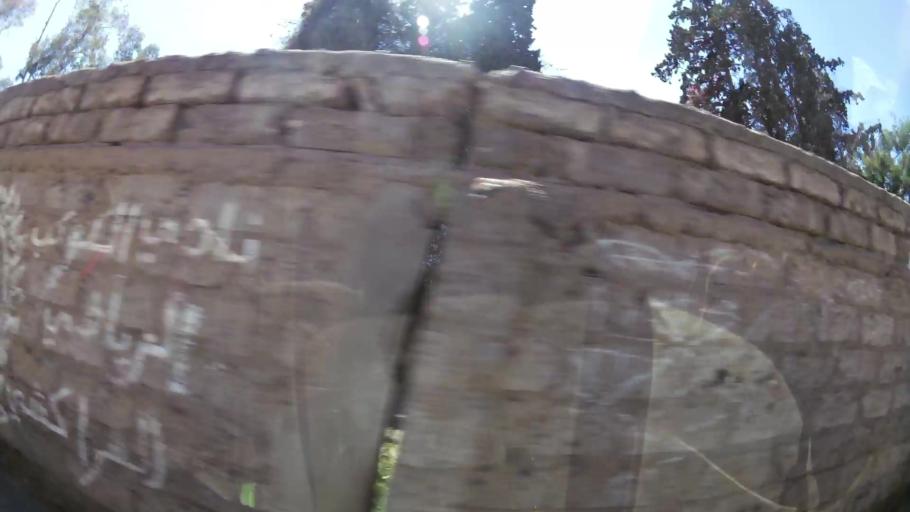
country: MA
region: Marrakech-Tensift-Al Haouz
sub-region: Marrakech
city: Marrakesh
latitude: 31.6376
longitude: -8.0465
